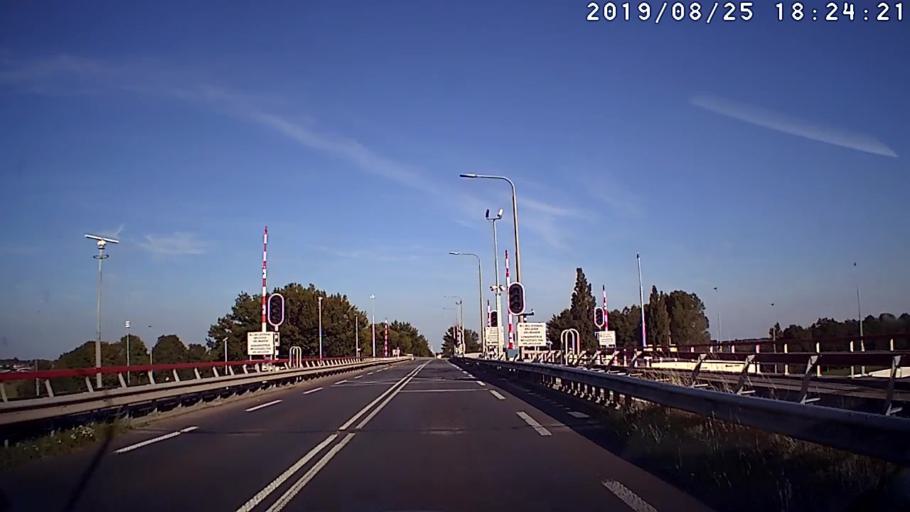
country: NL
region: Friesland
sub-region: Gemeente Lemsterland
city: Lemmer
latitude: 52.8530
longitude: 5.6753
